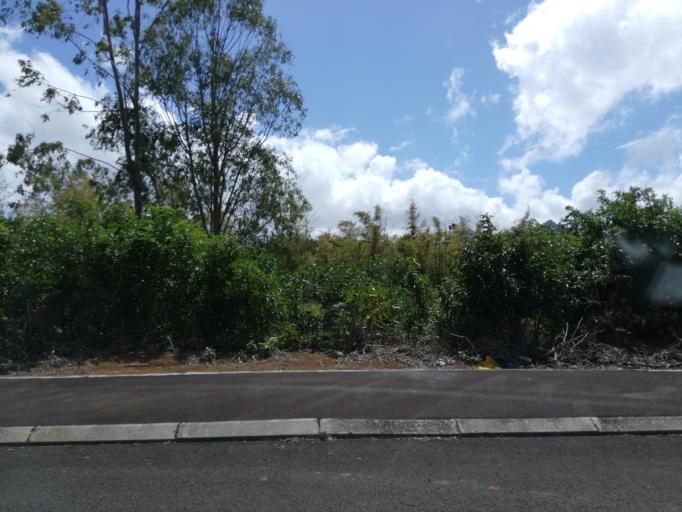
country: MU
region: Plaines Wilhems
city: Ebene
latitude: -20.2381
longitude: 57.4875
